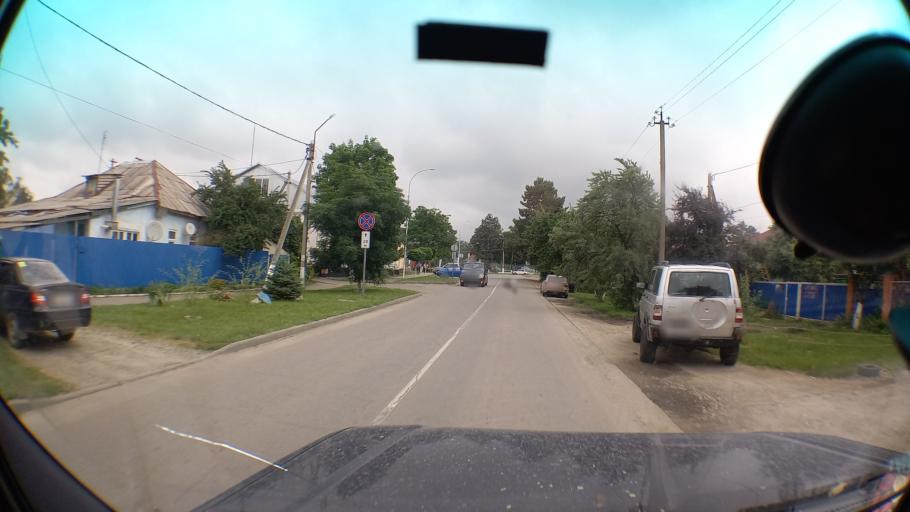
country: RU
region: Krasnodarskiy
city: Mostovskoy
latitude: 44.4103
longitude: 40.8031
